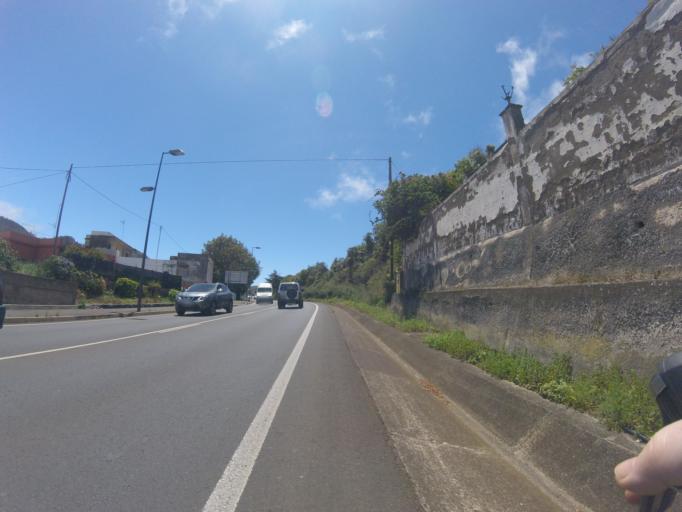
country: ES
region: Canary Islands
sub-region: Provincia de Santa Cruz de Tenerife
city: Tegueste
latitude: 28.5181
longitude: -16.3236
